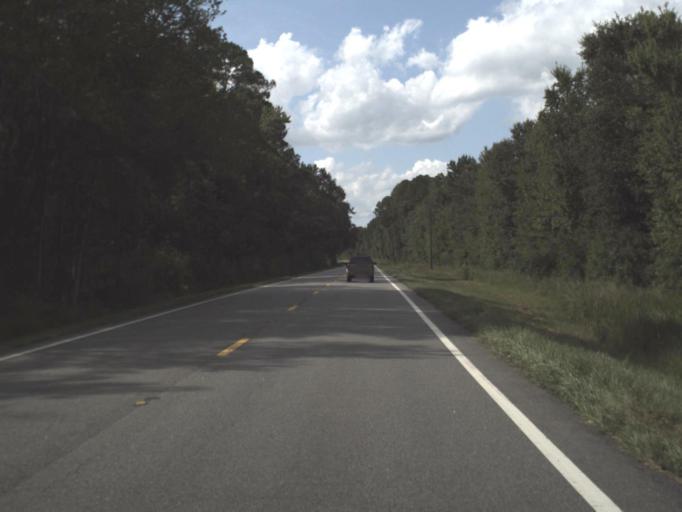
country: US
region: Florida
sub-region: Taylor County
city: Perry
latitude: 30.3376
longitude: -83.6455
